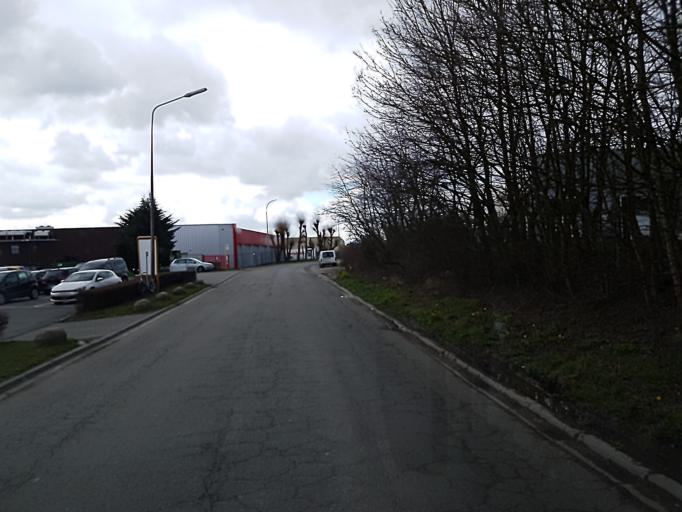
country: BE
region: Flanders
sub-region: Provincie Vlaams-Brabant
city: Ternat
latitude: 50.8889
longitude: 4.1751
